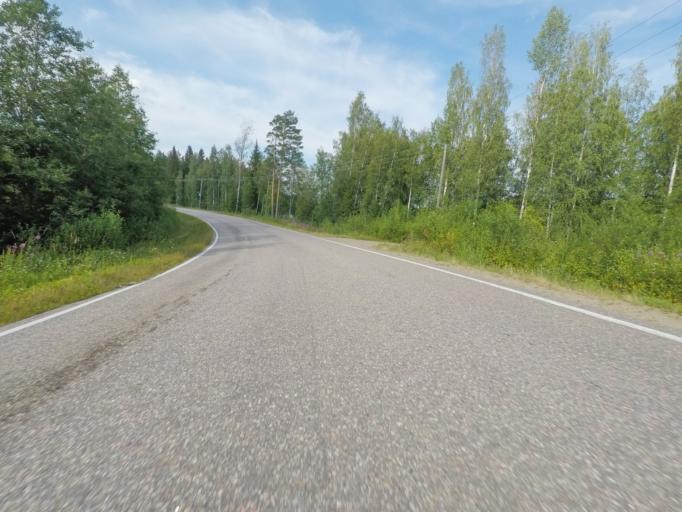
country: FI
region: Southern Savonia
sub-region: Savonlinna
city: Sulkava
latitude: 61.7312
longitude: 28.2107
